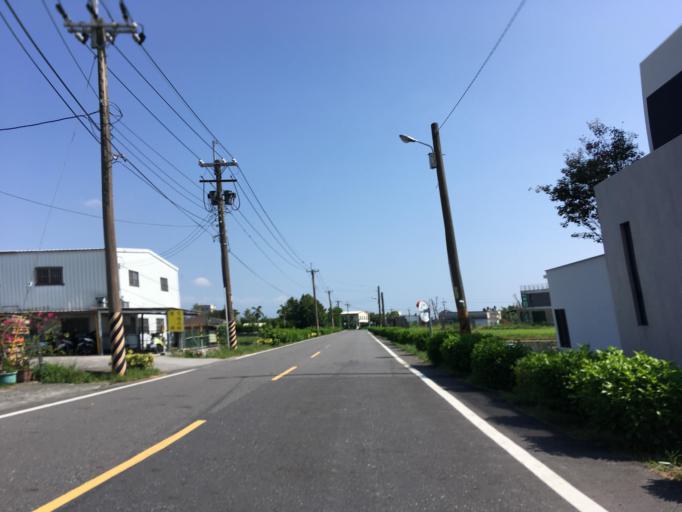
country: TW
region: Taiwan
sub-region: Yilan
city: Yilan
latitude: 24.6773
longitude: 121.7340
